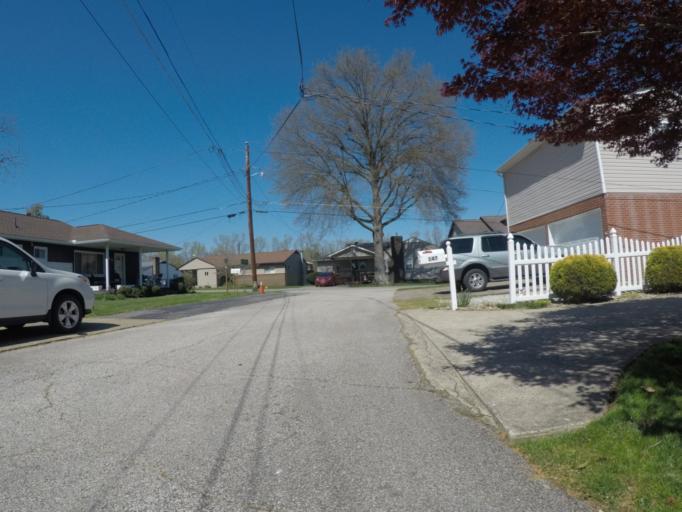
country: US
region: West Virginia
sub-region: Cabell County
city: Pea Ridge
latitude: 38.4143
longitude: -82.3094
